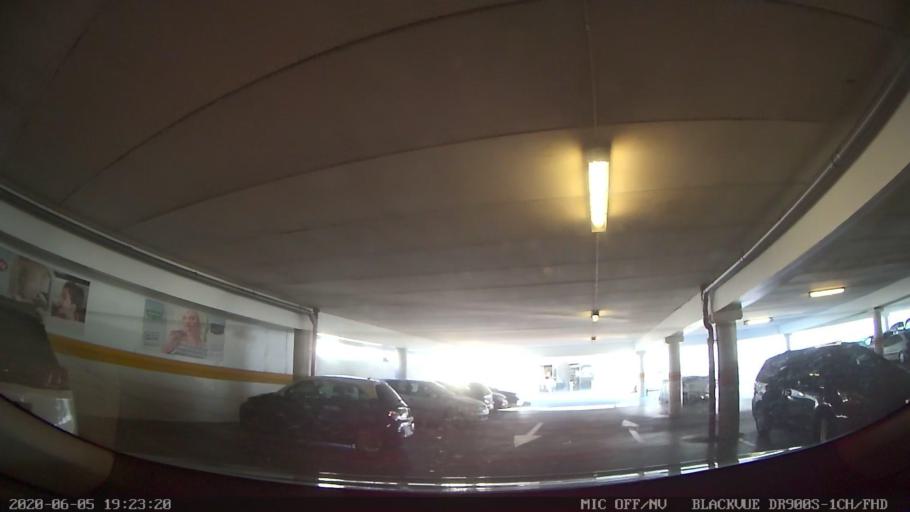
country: PT
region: Porto
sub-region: Valongo
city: Ermesinde
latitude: 41.2136
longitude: -8.5506
